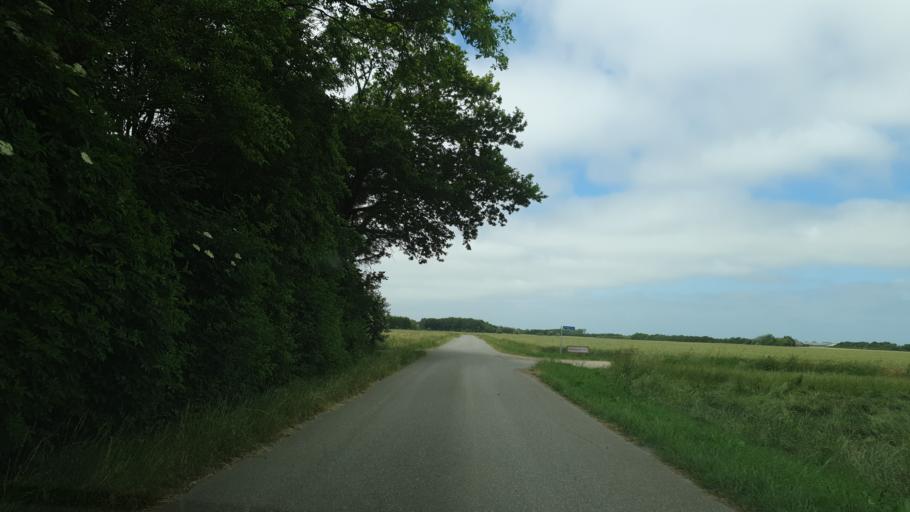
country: DK
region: Central Jutland
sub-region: Ringkobing-Skjern Kommune
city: Skjern
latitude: 55.9349
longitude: 8.4020
